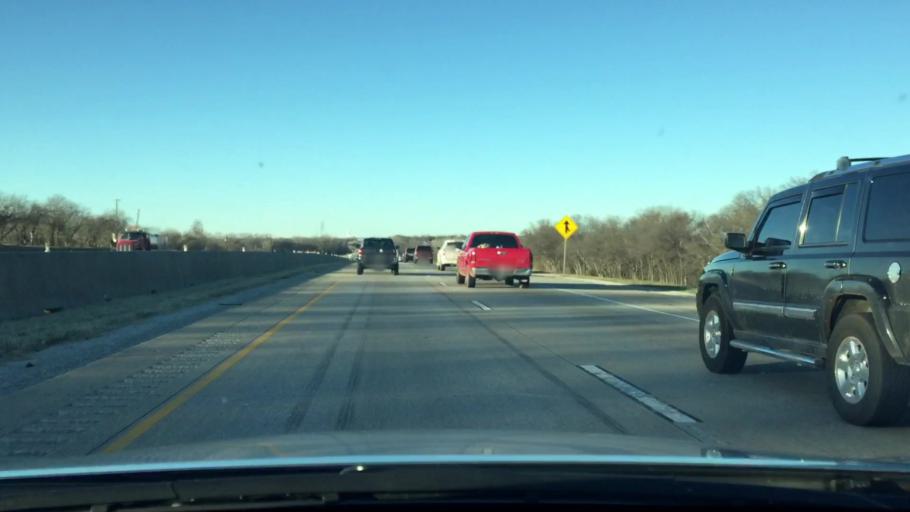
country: US
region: Texas
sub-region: Denton County
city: Sanger
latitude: 33.3262
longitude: -97.1805
